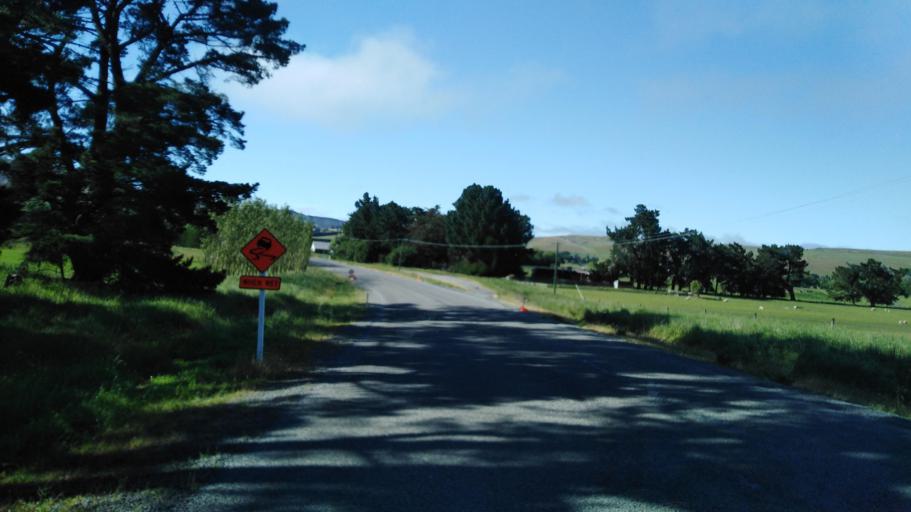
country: NZ
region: Canterbury
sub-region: Hurunui District
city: Amberley
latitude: -42.9502
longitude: 172.7076
